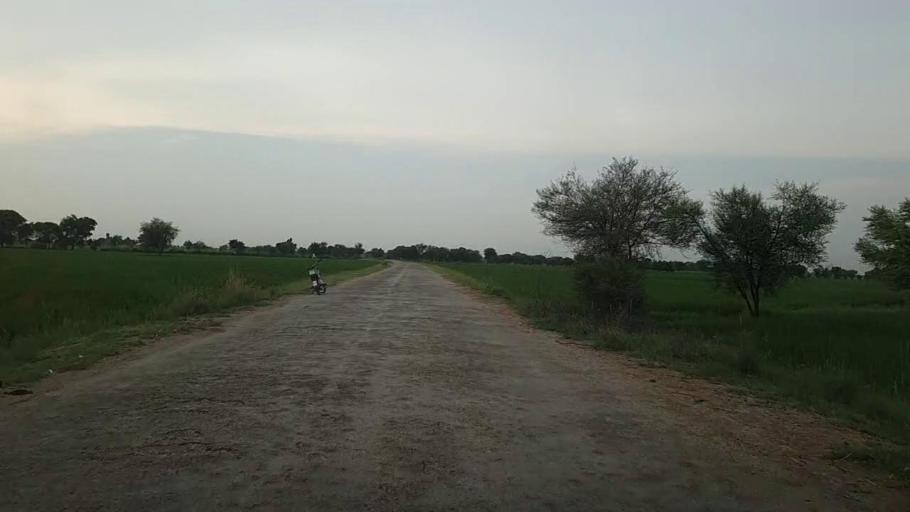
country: PK
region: Sindh
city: Khanpur
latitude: 27.8406
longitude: 69.4668
